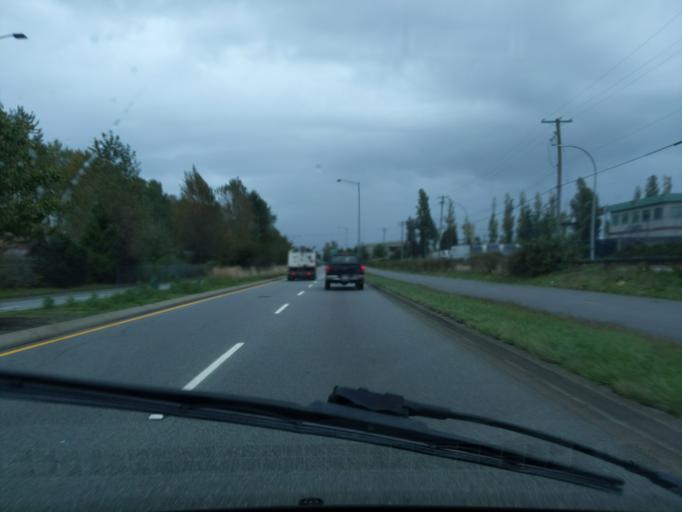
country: CA
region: British Columbia
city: Pitt Meadows
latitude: 49.1808
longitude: -122.6989
